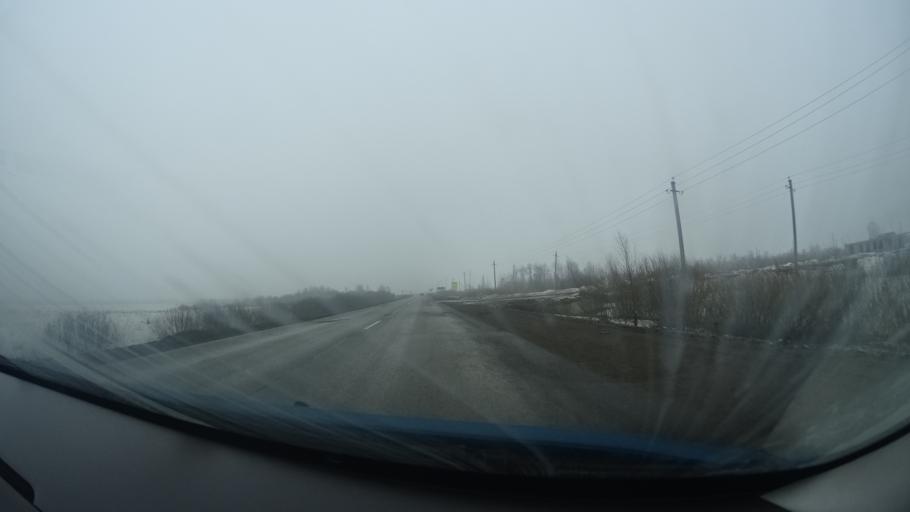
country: RU
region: Perm
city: Kuyeda
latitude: 56.4467
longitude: 55.5943
